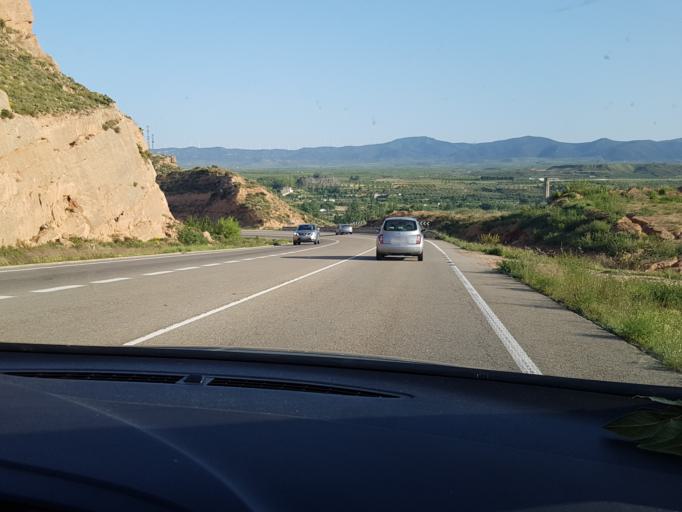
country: ES
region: La Rioja
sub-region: Provincia de La Rioja
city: Arnedo
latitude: 42.2344
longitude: -2.0818
